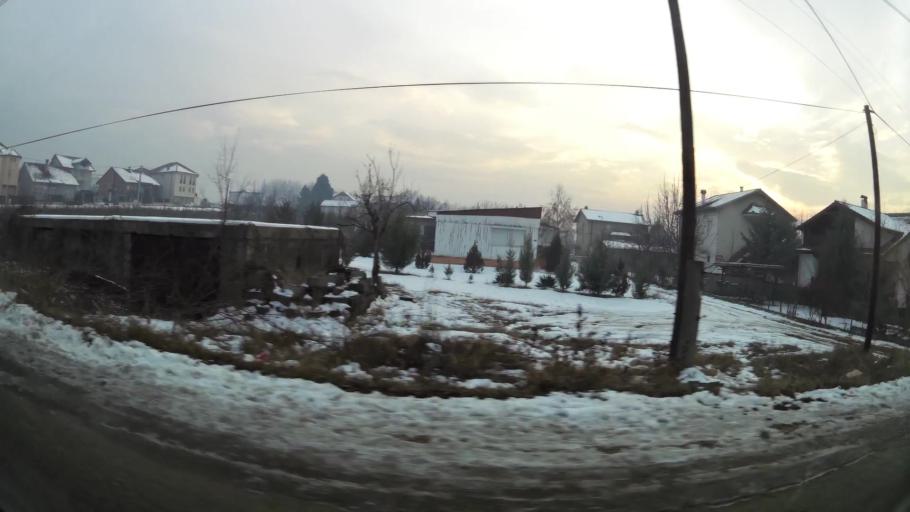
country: MK
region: Suto Orizari
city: Suto Orizare
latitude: 42.0358
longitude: 21.4125
